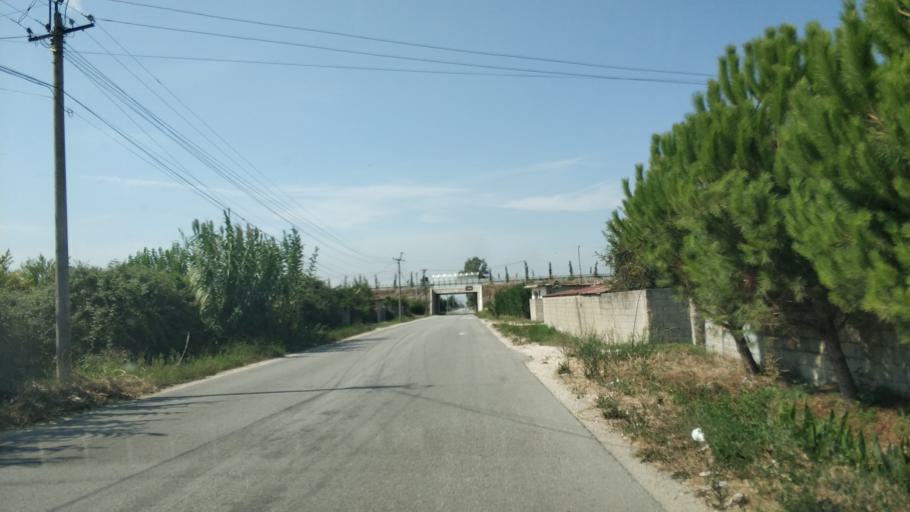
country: AL
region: Fier
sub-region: Rrethi i Fierit
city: Dermenas
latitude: 40.7422
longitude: 19.5033
